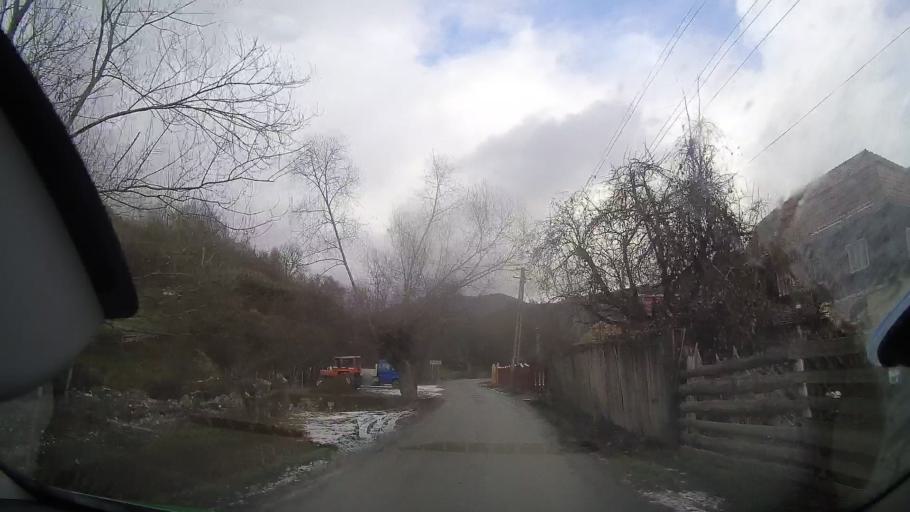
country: RO
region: Alba
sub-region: Comuna Ocolis
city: Ocolis
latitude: 46.4976
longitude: 23.4534
